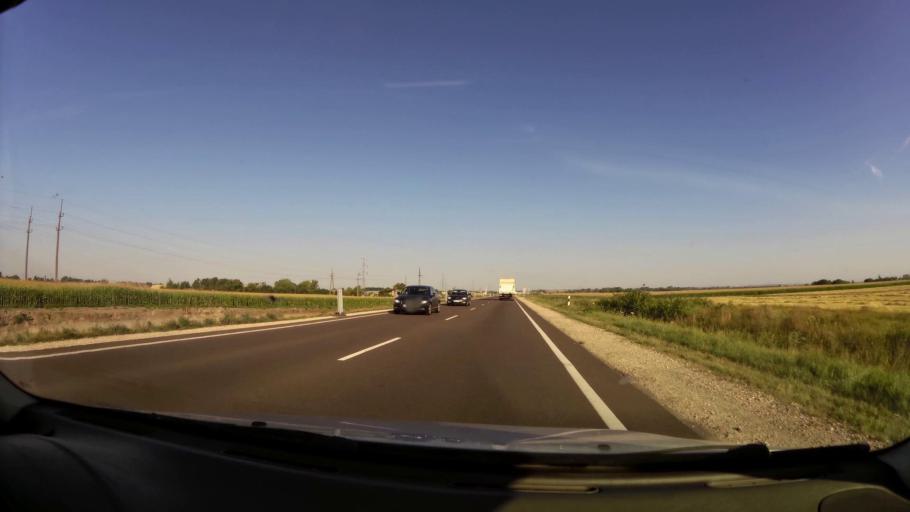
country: HU
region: Pest
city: Cegled
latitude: 47.1978
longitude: 19.8046
